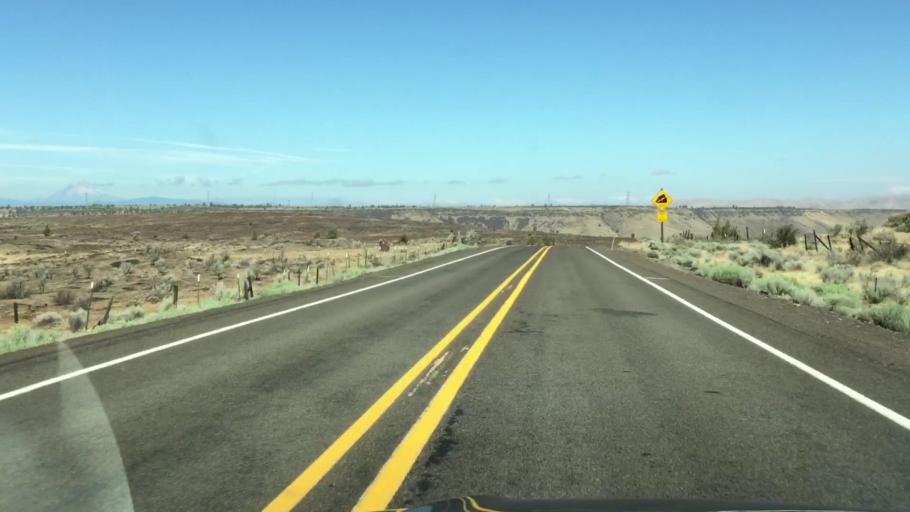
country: US
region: Oregon
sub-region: Jefferson County
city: Warm Springs
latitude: 45.1590
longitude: -121.0700
